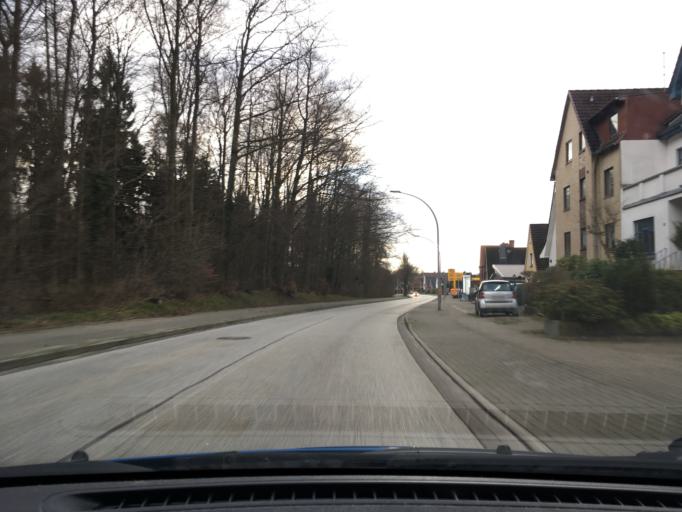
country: DE
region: Schleswig-Holstein
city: Heiligenstedten
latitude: 53.9428
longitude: 9.4970
